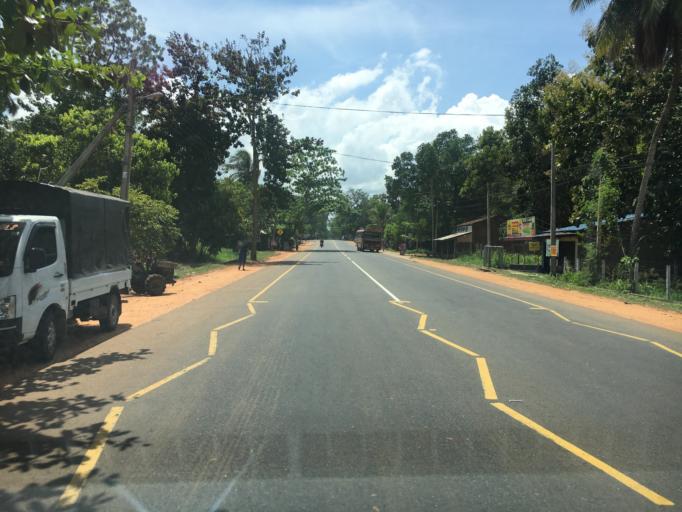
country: LK
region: North Central
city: Anuradhapura
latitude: 8.2709
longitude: 80.5015
